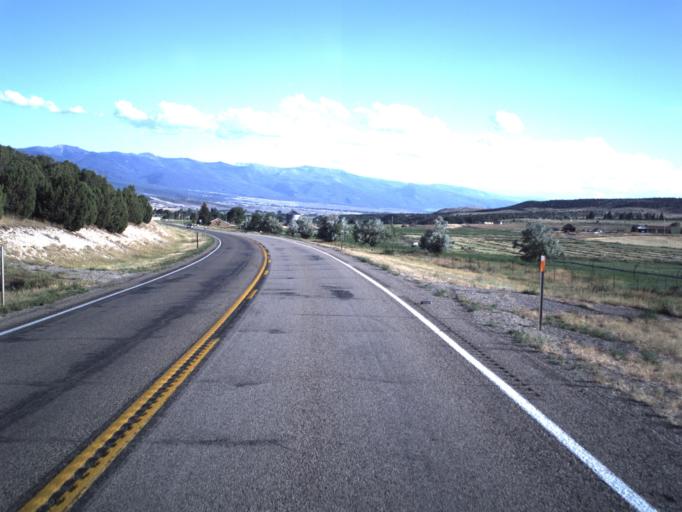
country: US
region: Utah
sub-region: Sanpete County
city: Fairview
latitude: 39.6489
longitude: -111.4511
